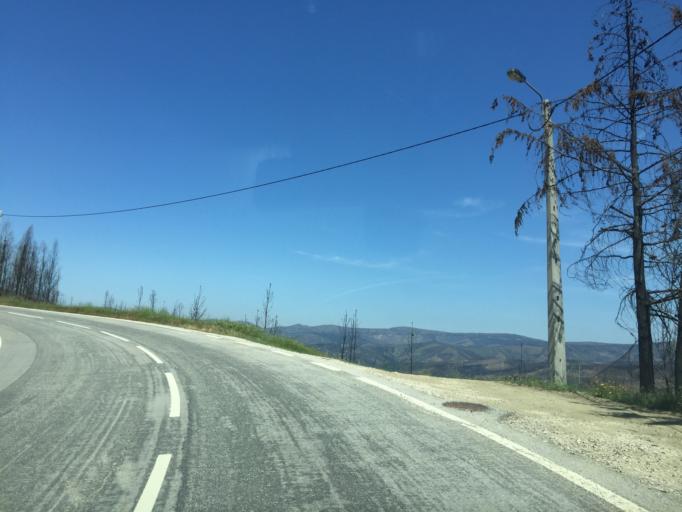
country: PT
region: Coimbra
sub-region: Pampilhosa da Serra
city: Pampilhosa da Serra
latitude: 40.0309
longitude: -7.9670
